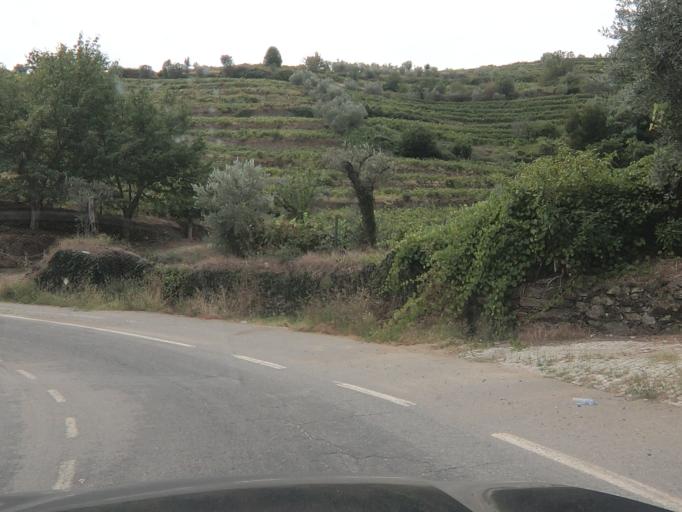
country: PT
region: Vila Real
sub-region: Santa Marta de Penaguiao
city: Santa Marta de Penaguiao
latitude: 41.2213
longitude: -7.7751
